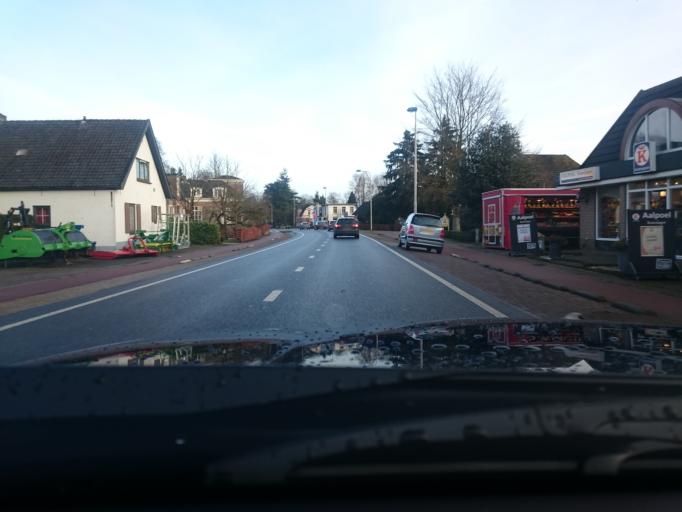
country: NL
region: Gelderland
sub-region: Gemeente Voorst
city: Voorst
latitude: 52.1679
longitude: 6.1436
